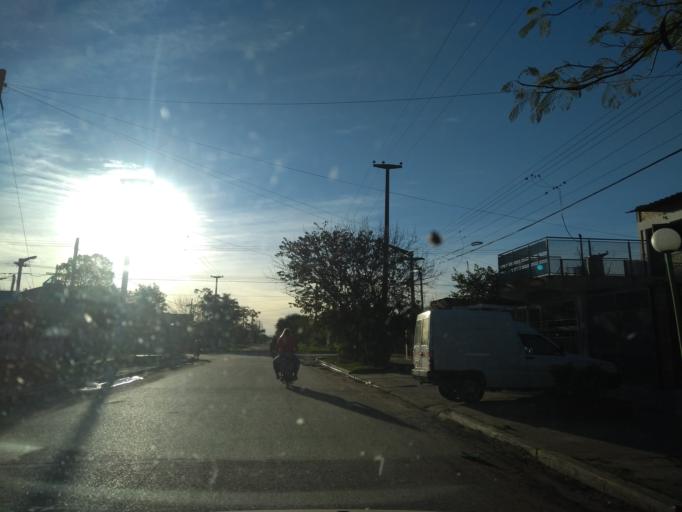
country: AR
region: Chaco
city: Barranqueras
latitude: -27.4961
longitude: -58.9554
